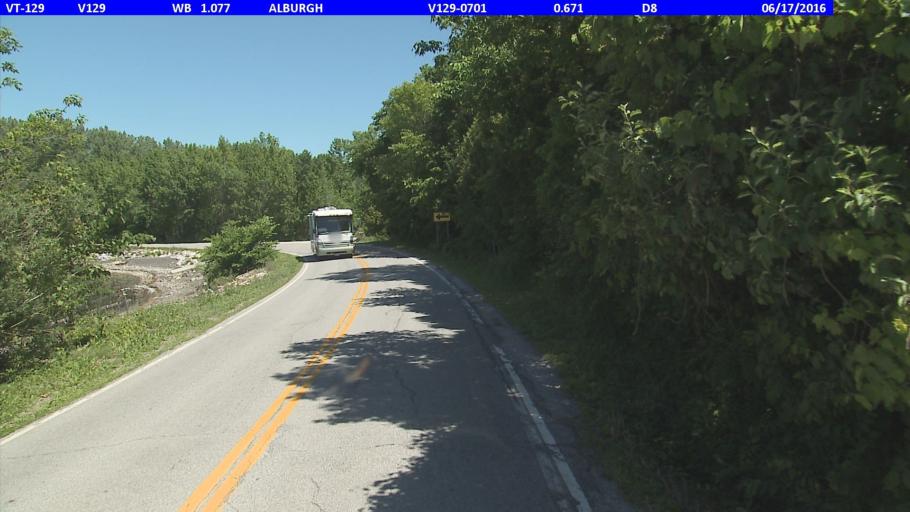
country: US
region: Vermont
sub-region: Grand Isle County
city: North Hero
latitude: 44.9019
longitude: -73.3040
